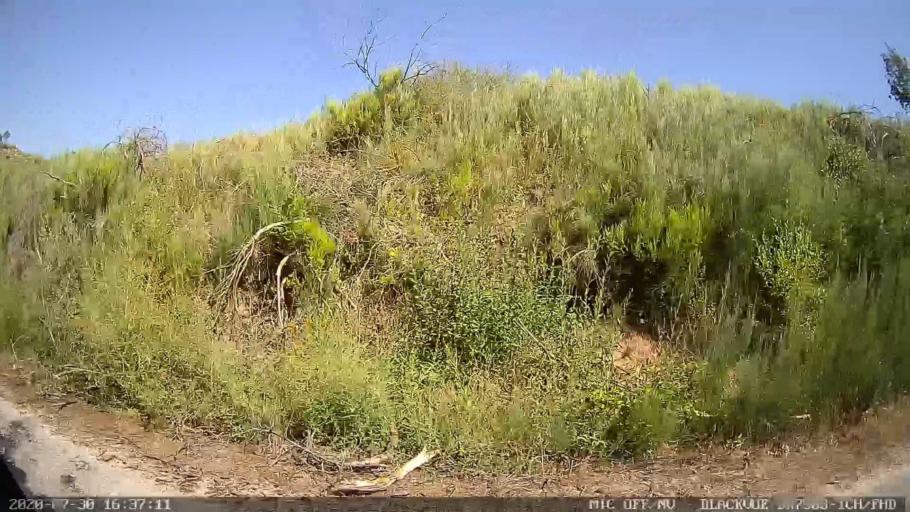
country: PT
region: Vila Real
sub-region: Sabrosa
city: Sabrosa
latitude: 41.3080
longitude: -7.4852
